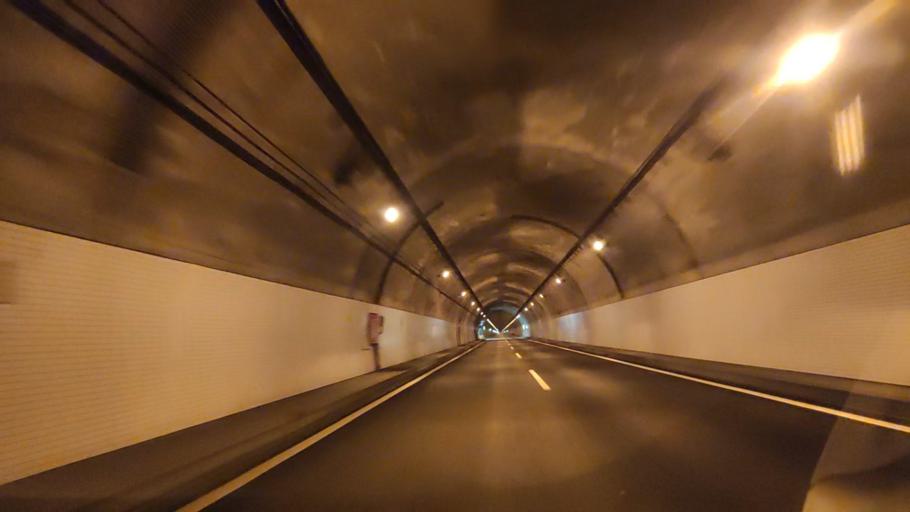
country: JP
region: Niigata
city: Itoigawa
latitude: 37.0087
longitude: 137.7532
